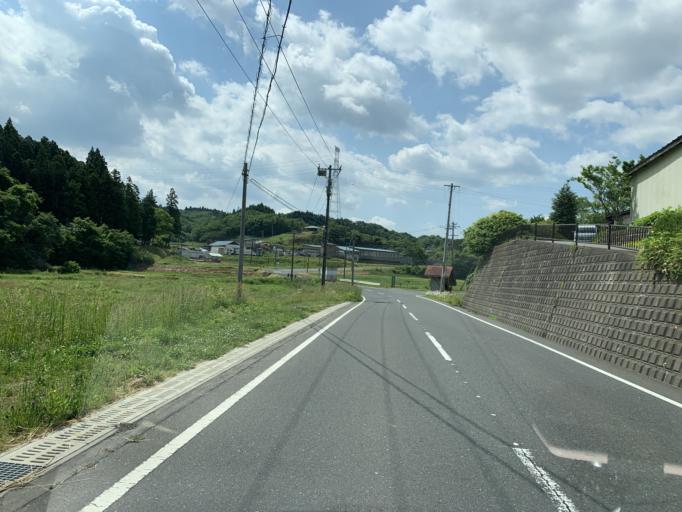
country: JP
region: Miyagi
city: Furukawa
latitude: 38.7827
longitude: 140.9583
